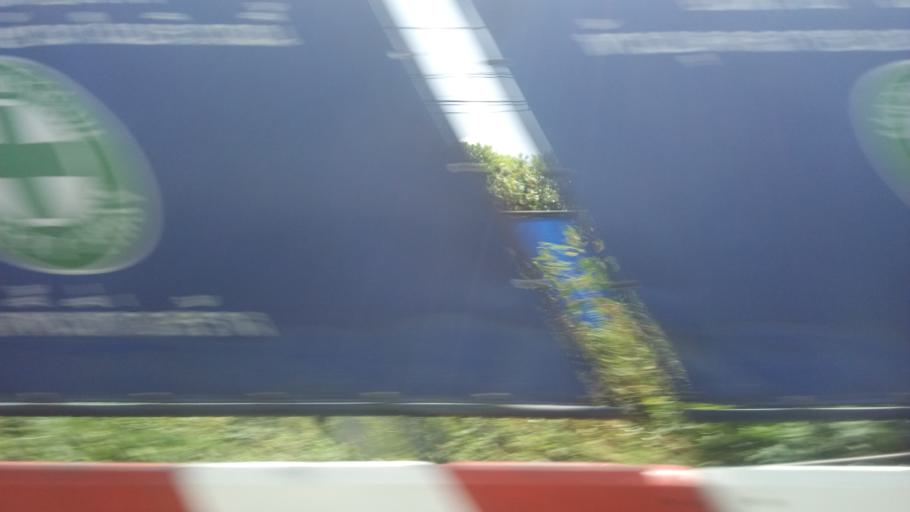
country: TH
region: Bangkok
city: Lak Si
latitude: 13.8906
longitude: 100.5677
